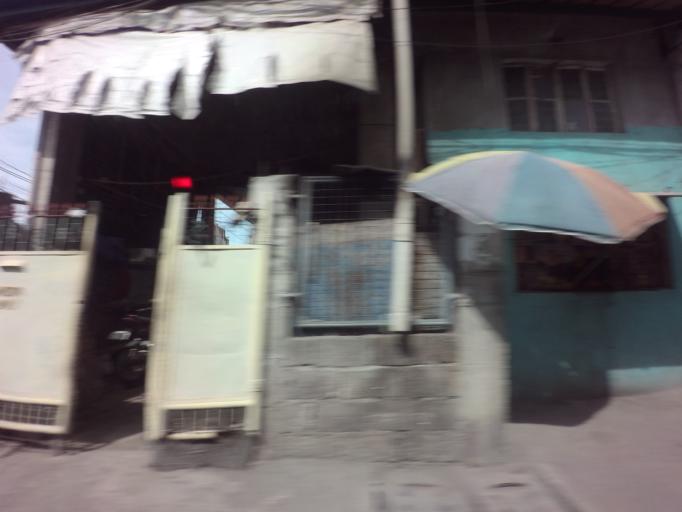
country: PH
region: Calabarzon
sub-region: Province of Rizal
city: Taguig
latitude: 14.5371
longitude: 121.0982
